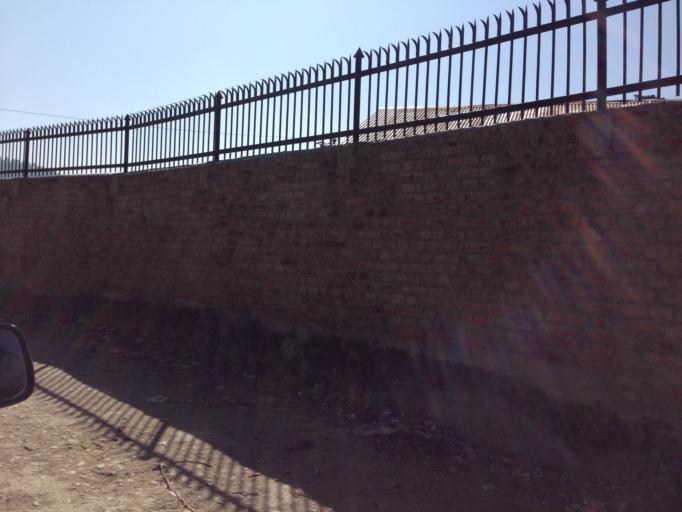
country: NP
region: Central Region
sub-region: Bagmati Zone
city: Kathmandu
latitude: 27.7786
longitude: 85.3648
